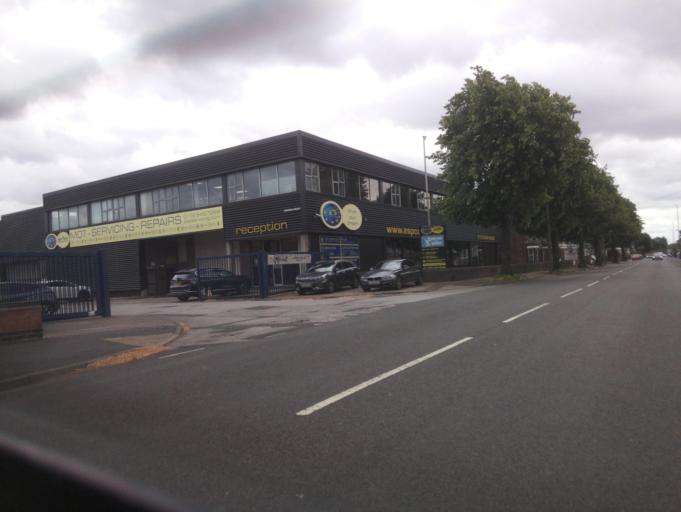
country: GB
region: England
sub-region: Derbyshire
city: Long Eaton
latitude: 52.8887
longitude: -1.2888
